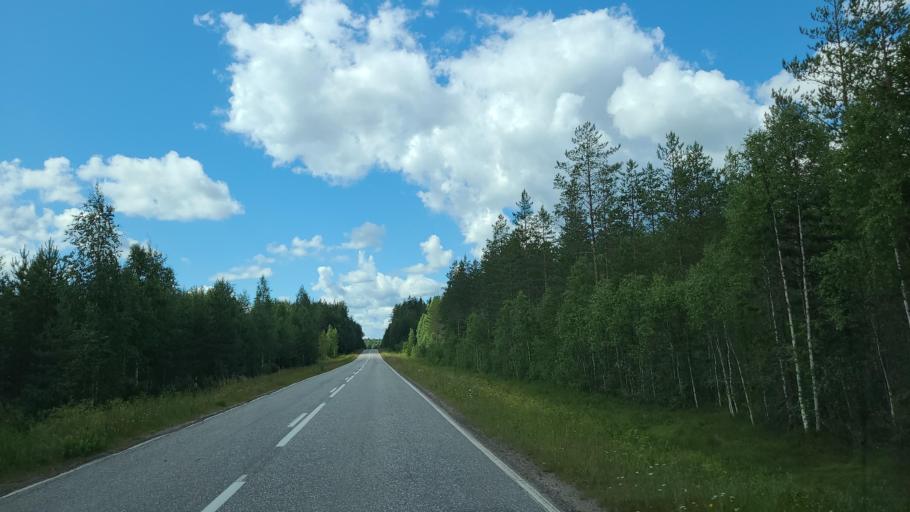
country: FI
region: Northern Savo
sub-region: Koillis-Savo
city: Kaavi
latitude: 62.9804
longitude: 28.7996
